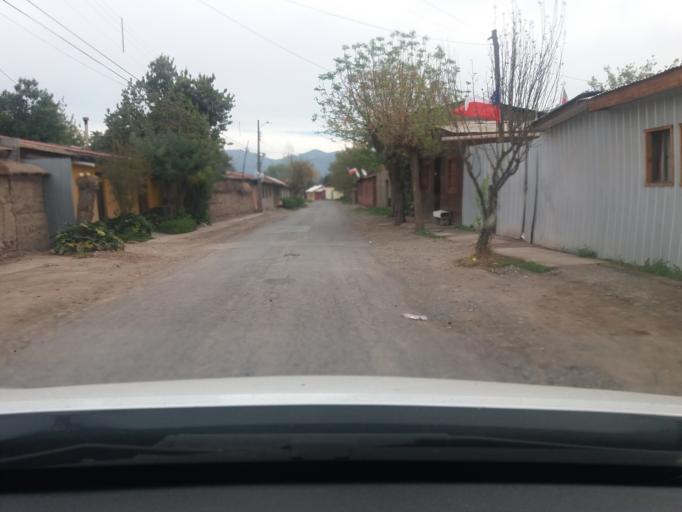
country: CL
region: Valparaiso
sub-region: Provincia de Los Andes
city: Los Andes
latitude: -32.8450
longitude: -70.6360
